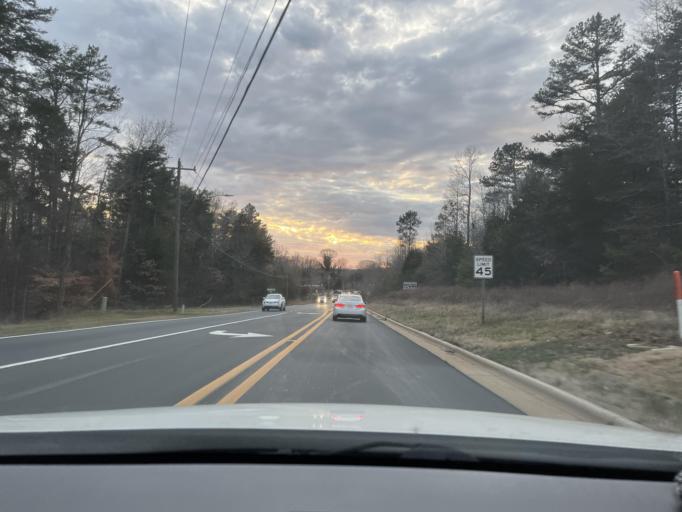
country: US
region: North Carolina
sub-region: Guilford County
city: Gibsonville
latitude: 36.0806
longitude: -79.5411
